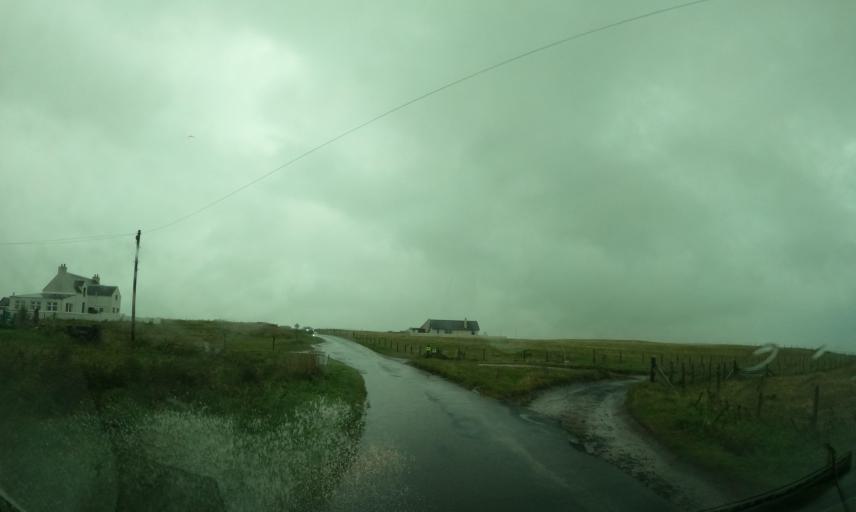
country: GB
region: Scotland
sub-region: Eilean Siar
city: Barra
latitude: 56.4717
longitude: -6.8992
